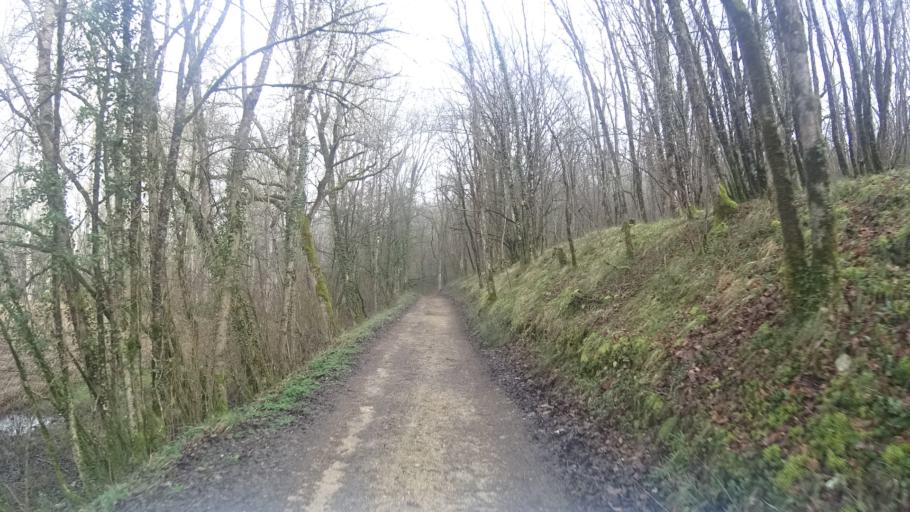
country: FR
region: Aquitaine
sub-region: Departement de la Dordogne
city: Terrasson-Lavilledieu
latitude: 45.0973
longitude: 1.2639
